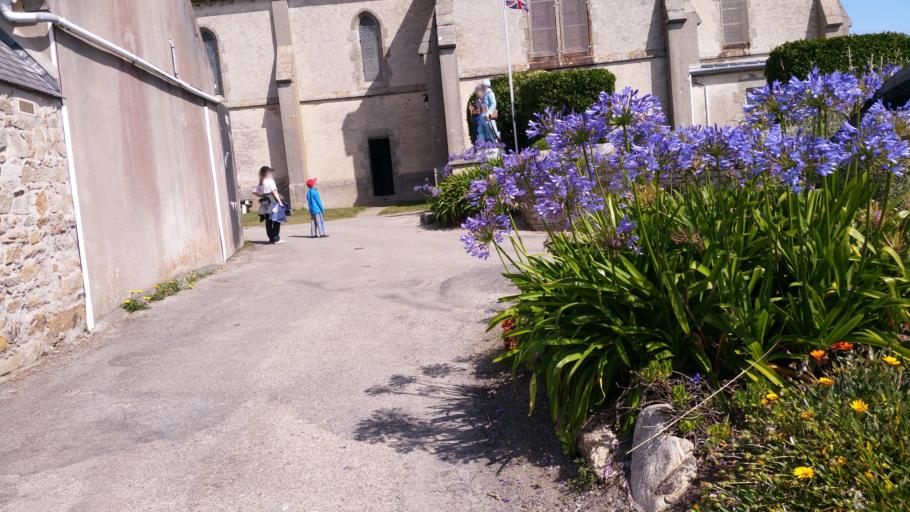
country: FR
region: Brittany
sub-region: Departement du Finistere
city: Le Conquet
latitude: 48.3956
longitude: -4.9579
